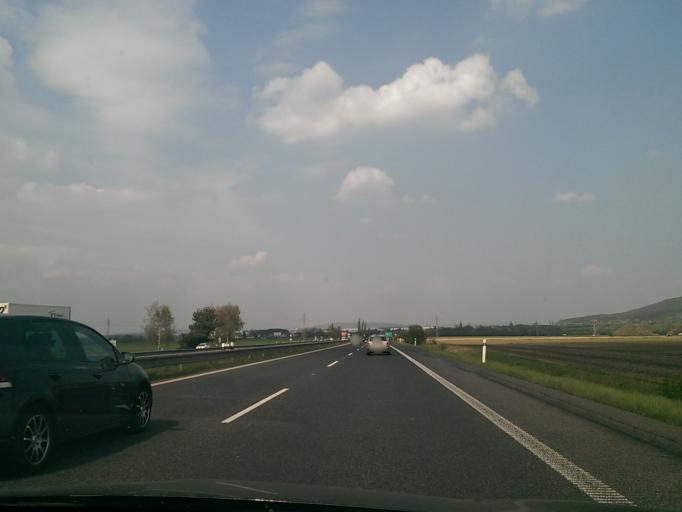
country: CZ
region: Central Bohemia
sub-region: Okres Mlada Boleslav
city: Mlada Boleslav
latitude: 50.3749
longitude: 14.8866
